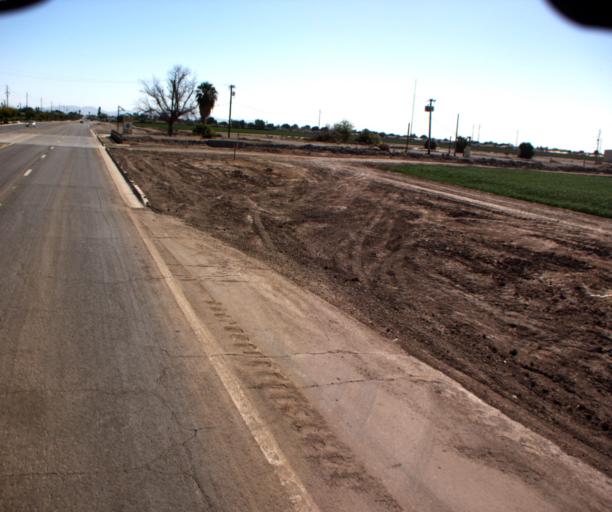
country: US
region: Arizona
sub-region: Yuma County
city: Somerton
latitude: 32.5967
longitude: -114.7278
